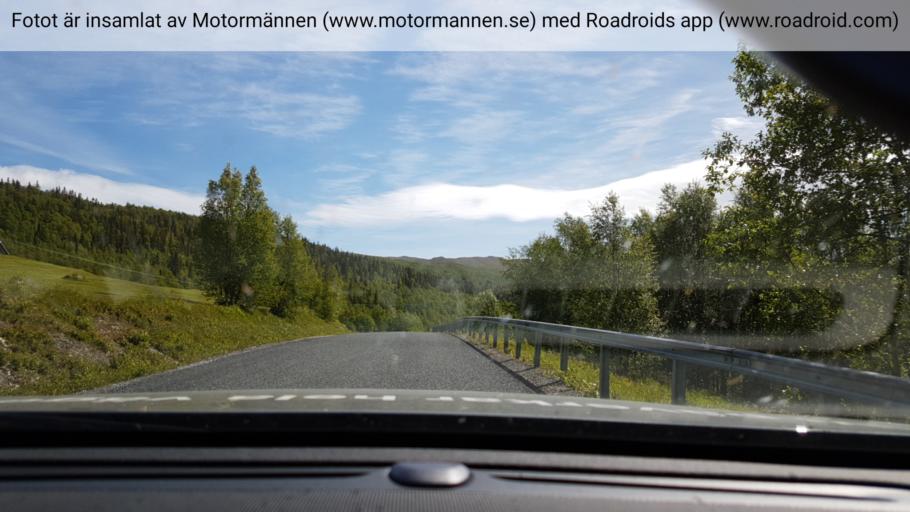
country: SE
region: Vaesterbotten
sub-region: Vilhelmina Kommun
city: Sjoberg
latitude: 65.3221
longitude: 15.2794
